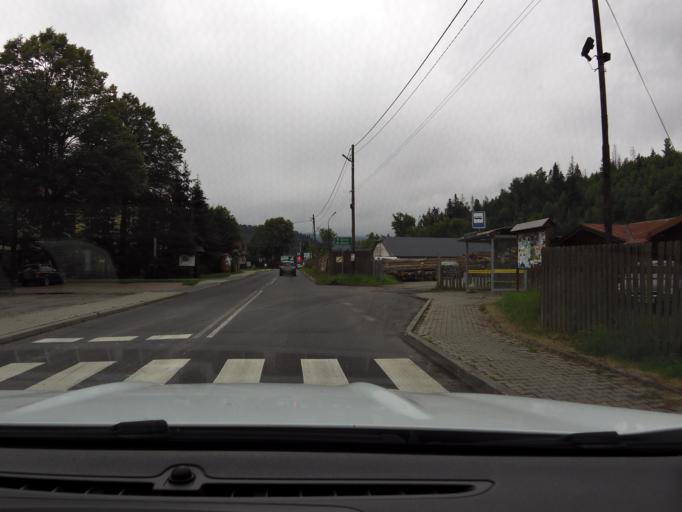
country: PL
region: Silesian Voivodeship
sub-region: Powiat zywiecki
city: Ujsoly
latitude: 49.4789
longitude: 19.1425
